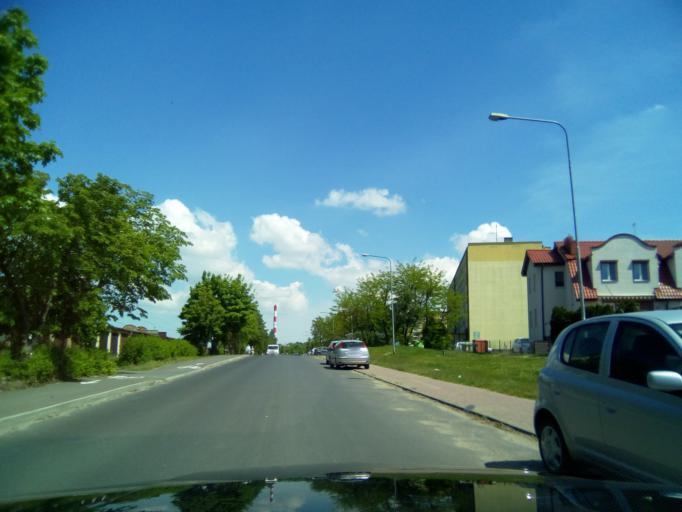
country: PL
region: Greater Poland Voivodeship
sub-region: Powiat gnieznienski
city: Gniezno
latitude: 52.5522
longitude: 17.5996
